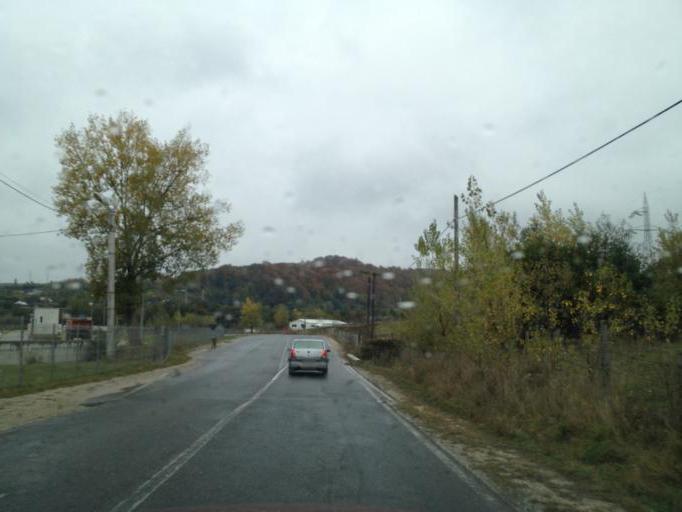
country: RO
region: Arges
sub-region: Comuna Valea Mare-Pravat
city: Valea Mare Pravat
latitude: 45.2939
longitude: 25.1132
